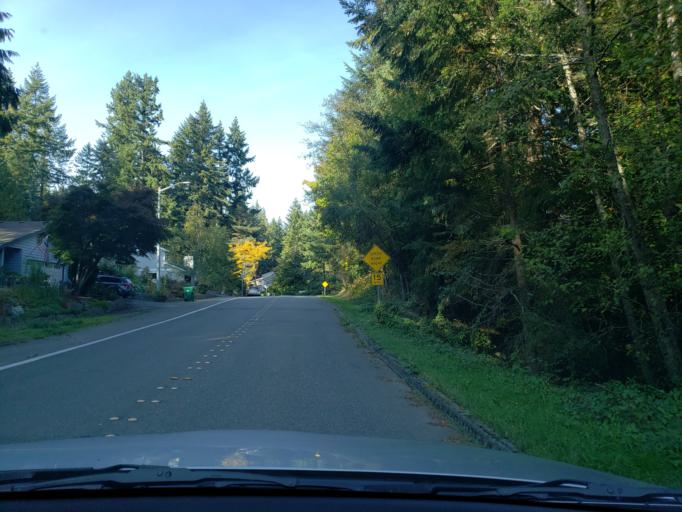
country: US
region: Washington
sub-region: Snohomish County
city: Meadowdale
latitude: 47.8677
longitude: -122.3145
